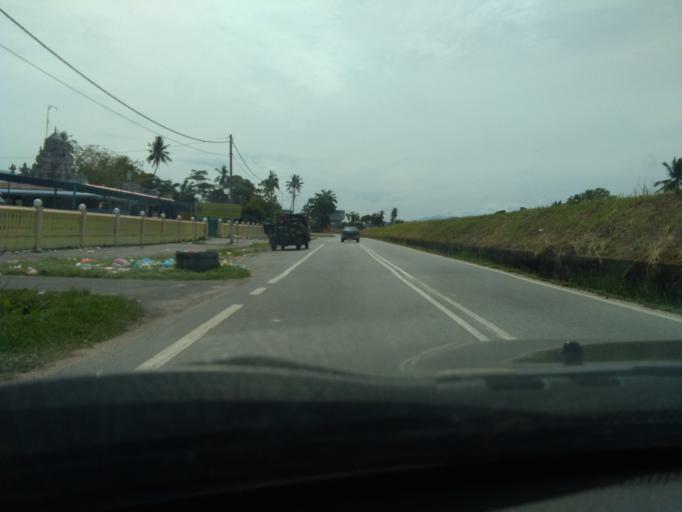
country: MY
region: Perak
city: Bagan Serai
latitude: 5.0137
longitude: 100.5361
